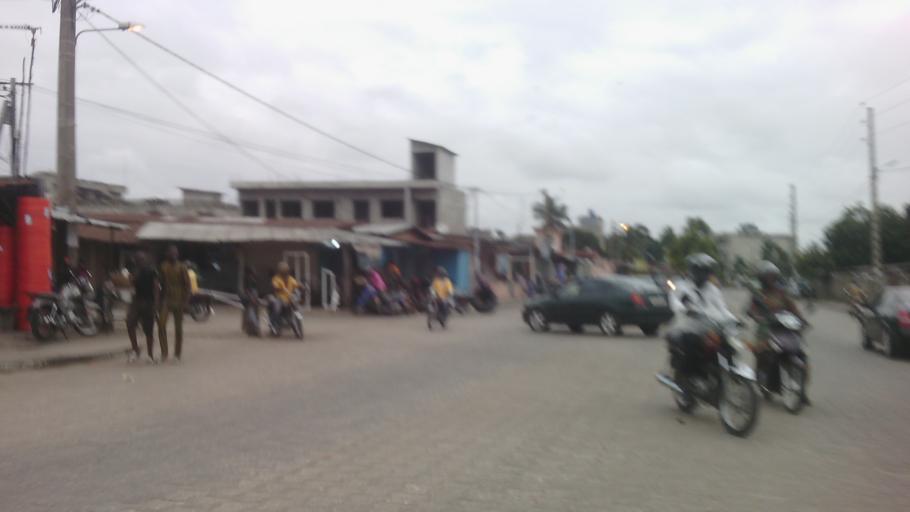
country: BJ
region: Littoral
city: Cotonou
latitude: 6.3920
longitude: 2.3675
